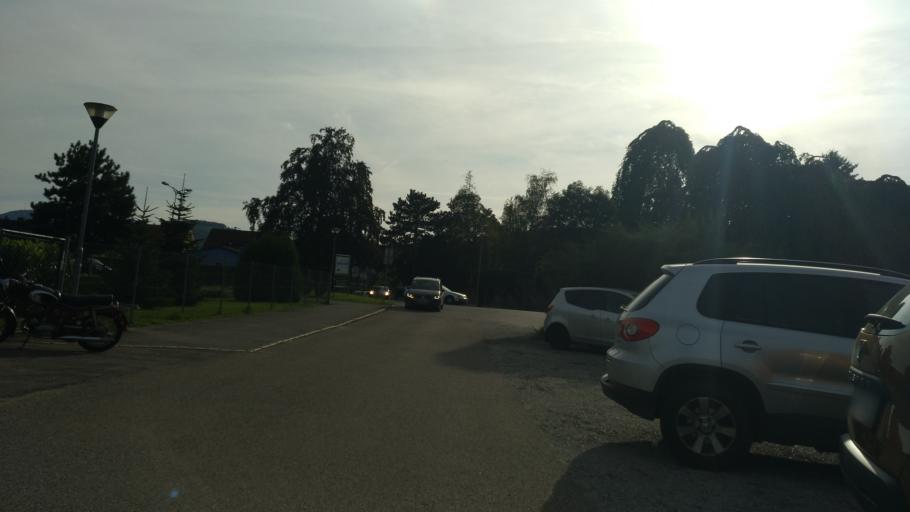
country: AT
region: Lower Austria
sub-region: Politischer Bezirk Sankt Polten
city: Wilhelmsburg
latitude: 48.0987
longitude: 15.6019
